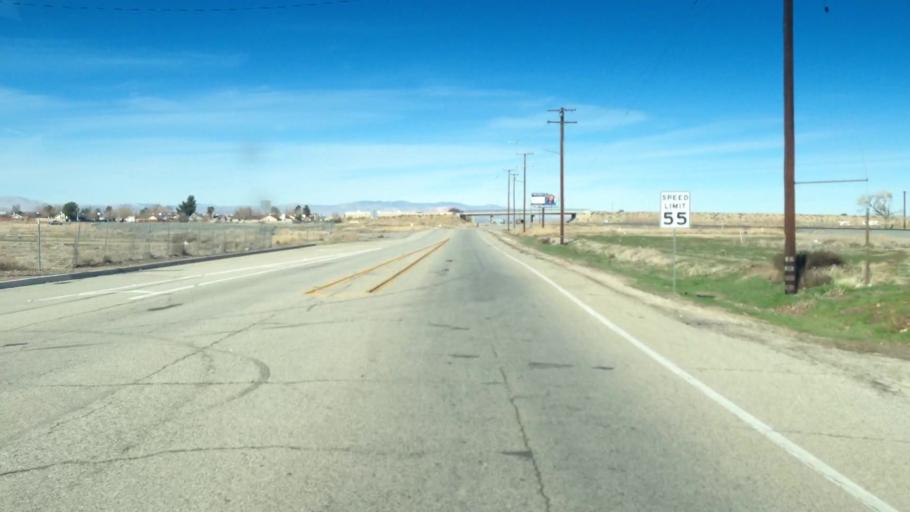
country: US
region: California
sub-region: Los Angeles County
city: Lancaster
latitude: 34.7122
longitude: -118.1391
